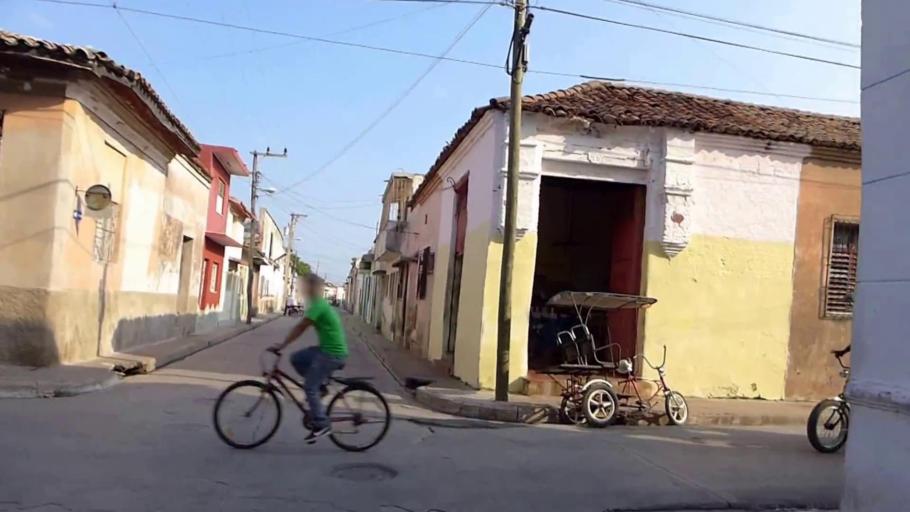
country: CU
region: Camaguey
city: Camaguey
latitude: 21.3776
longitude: -77.9213
